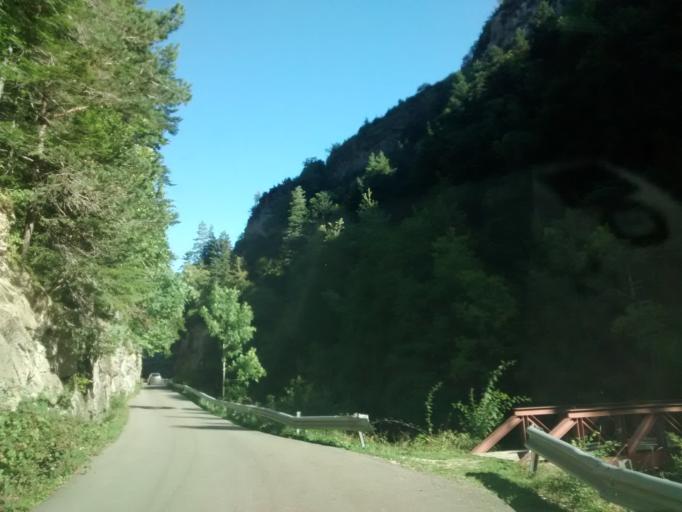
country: ES
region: Aragon
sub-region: Provincia de Huesca
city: Aragues del Puerto
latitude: 42.8212
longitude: -0.7116
